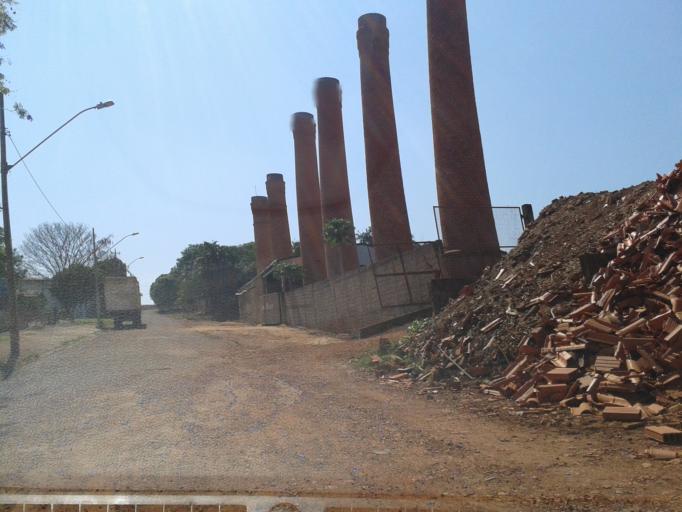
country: BR
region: Minas Gerais
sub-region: Ituiutaba
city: Ituiutaba
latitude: -18.9511
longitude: -49.4561
